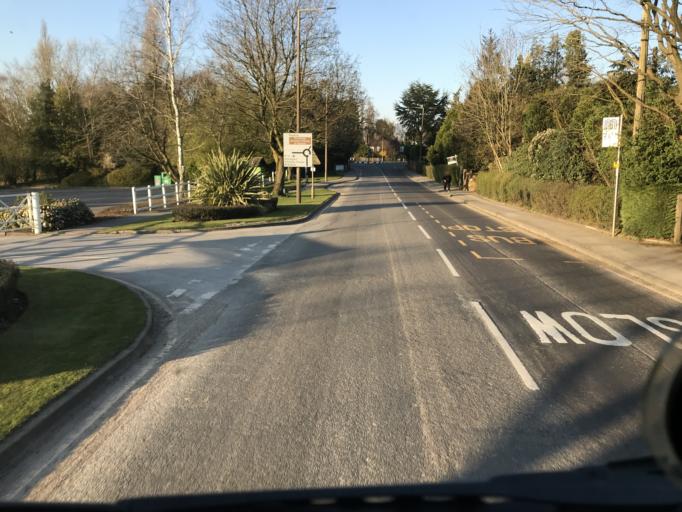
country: GB
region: England
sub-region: Borough of Stockport
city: Bramhall
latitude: 53.3435
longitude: -2.1588
